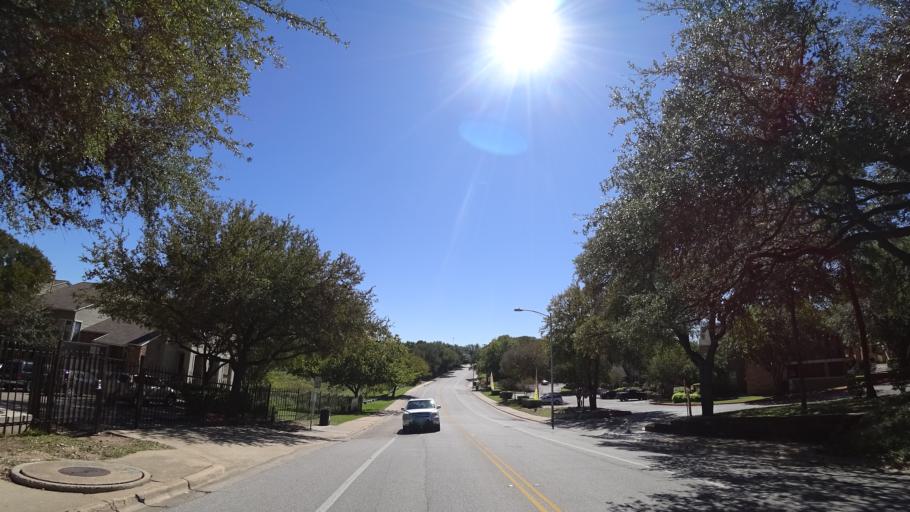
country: US
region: Texas
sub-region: Travis County
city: Austin
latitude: 30.2231
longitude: -97.7422
